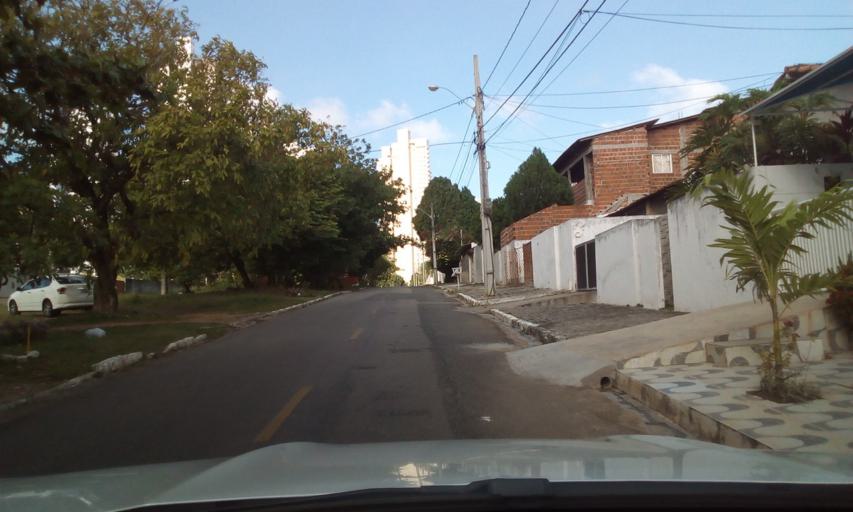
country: BR
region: Paraiba
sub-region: Joao Pessoa
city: Joao Pessoa
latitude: -7.1339
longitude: -34.8326
